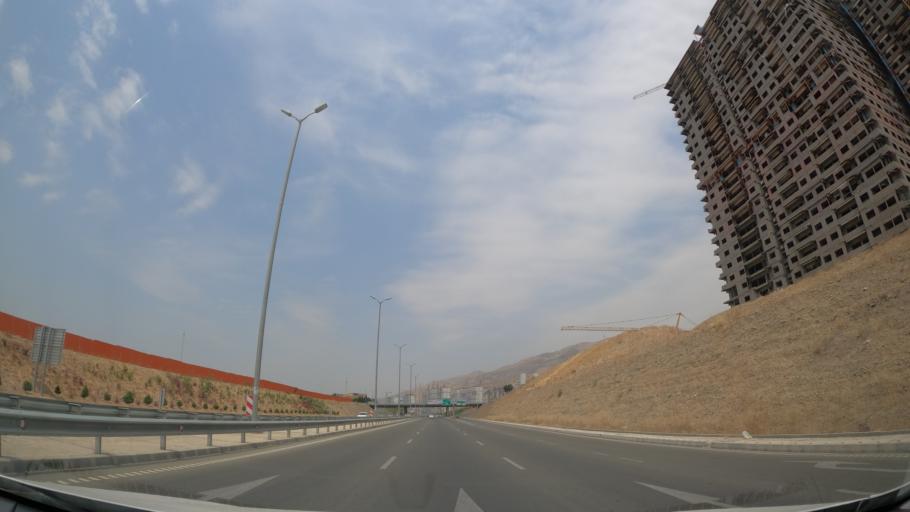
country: IR
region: Tehran
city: Shahr-e Qods
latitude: 35.7487
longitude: 51.1766
